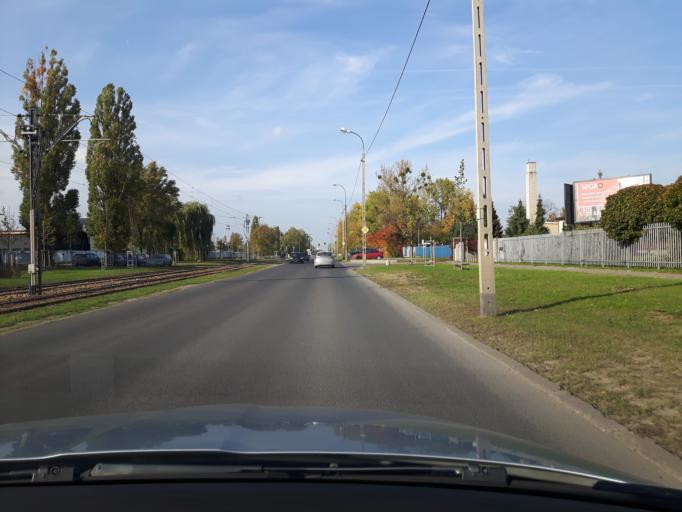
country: PL
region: Masovian Voivodeship
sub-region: Warszawa
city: Targowek
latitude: 52.3036
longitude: 21.0197
